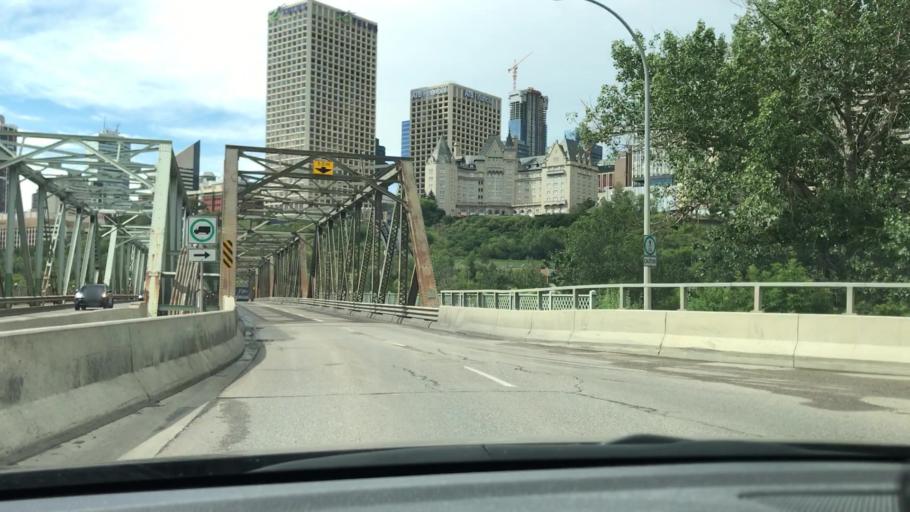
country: CA
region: Alberta
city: Edmonton
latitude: 53.5373
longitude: -113.4849
